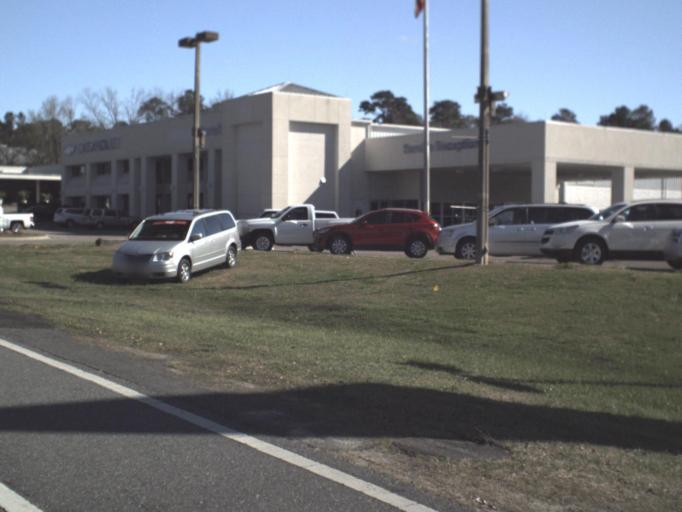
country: US
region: Florida
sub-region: Leon County
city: Tallahassee
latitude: 30.4580
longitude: -84.3497
